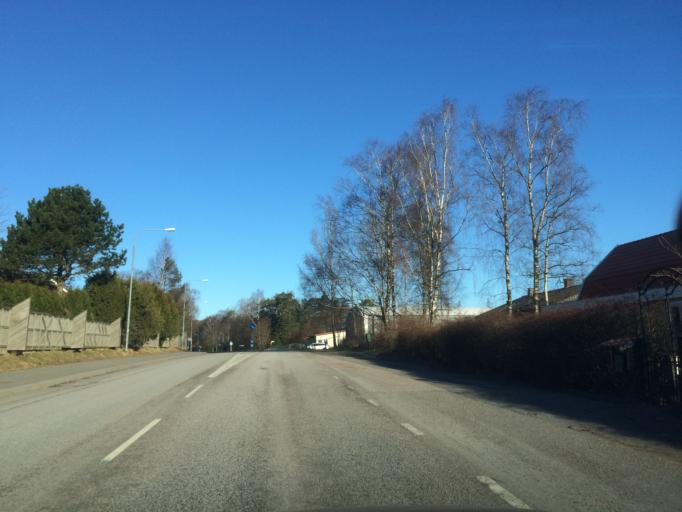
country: SE
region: Vaestra Goetaland
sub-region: Molndal
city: Lindome
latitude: 57.5869
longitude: 12.0710
